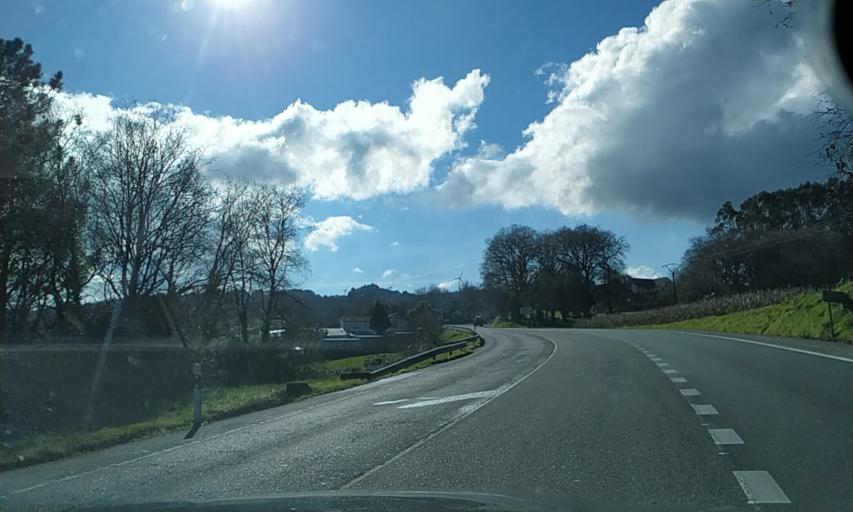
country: ES
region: Galicia
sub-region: Provincia de Pontevedra
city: Silleda
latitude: 42.7012
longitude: -8.3136
